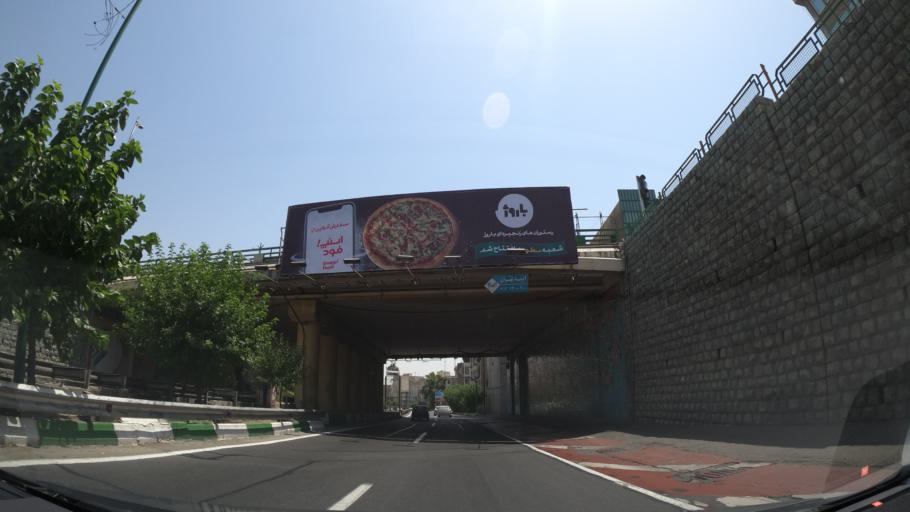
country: IR
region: Tehran
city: Tehran
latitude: 35.7244
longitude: 51.4247
